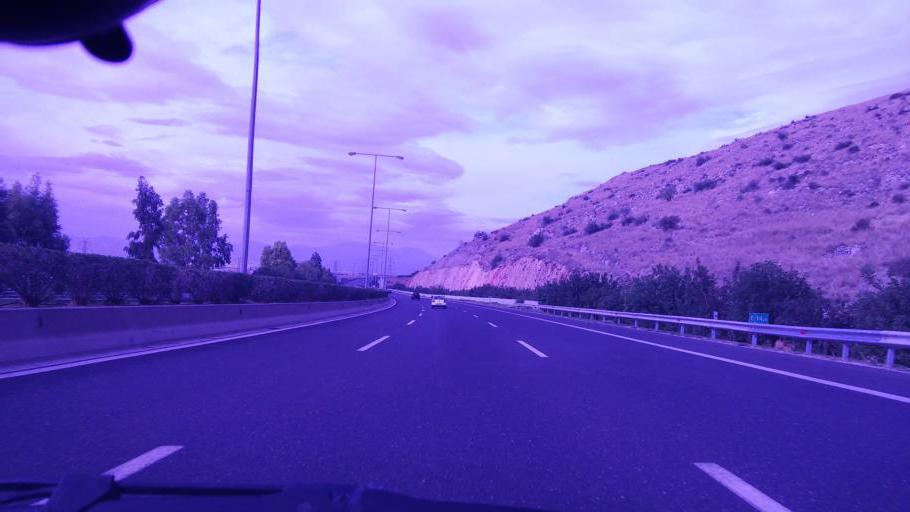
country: GR
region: Attica
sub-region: Nomarchia Dytikis Attikis
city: Fyli
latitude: 38.0864
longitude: 23.6572
